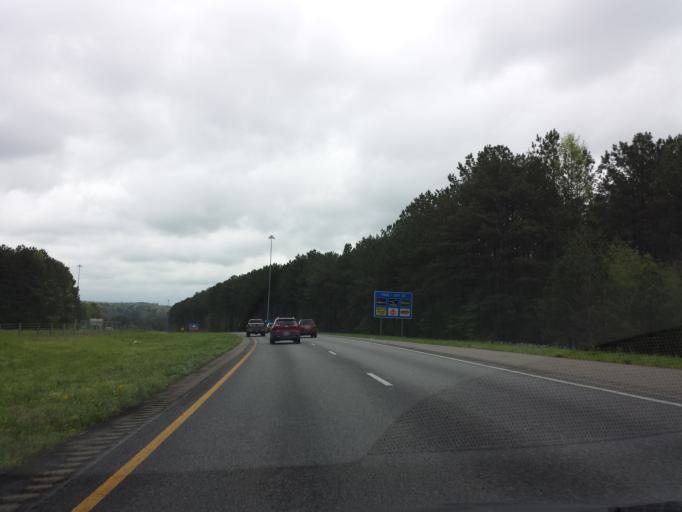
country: US
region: Georgia
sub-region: Cherokee County
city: Canton
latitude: 34.2394
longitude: -84.4657
